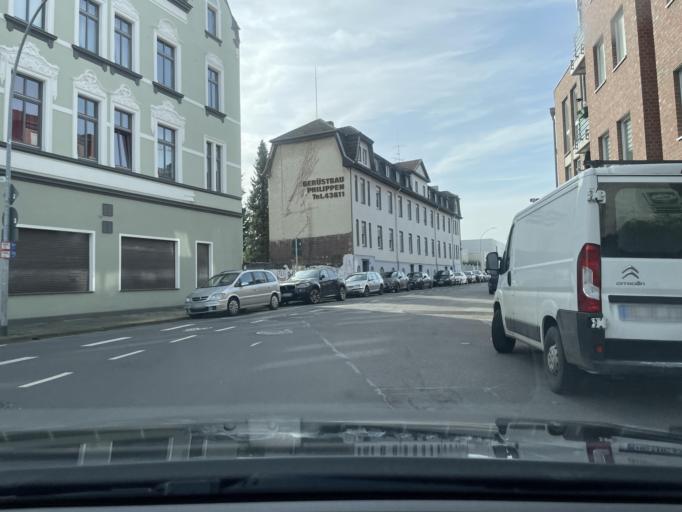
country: DE
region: North Rhine-Westphalia
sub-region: Regierungsbezirk Dusseldorf
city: Monchengladbach
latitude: 51.1983
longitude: 6.4578
